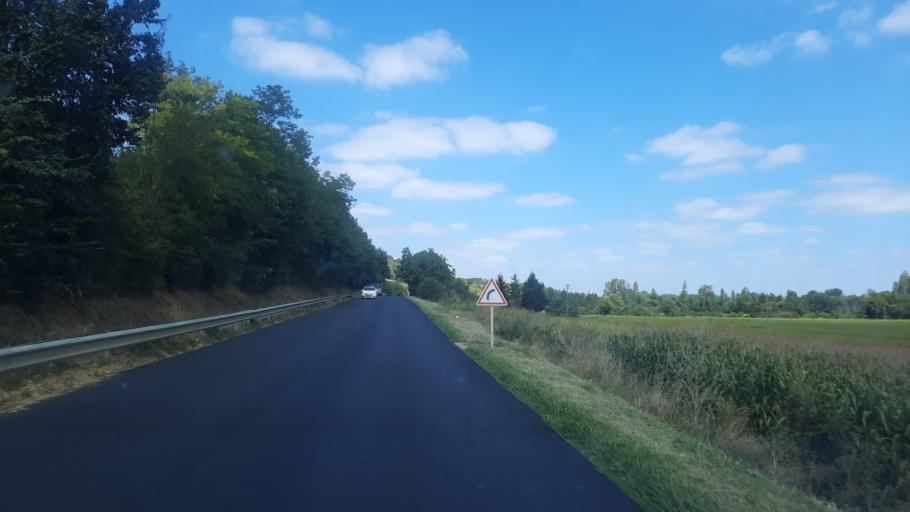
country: FR
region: Midi-Pyrenees
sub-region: Departement du Gers
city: Lombez
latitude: 43.4675
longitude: 0.8940
